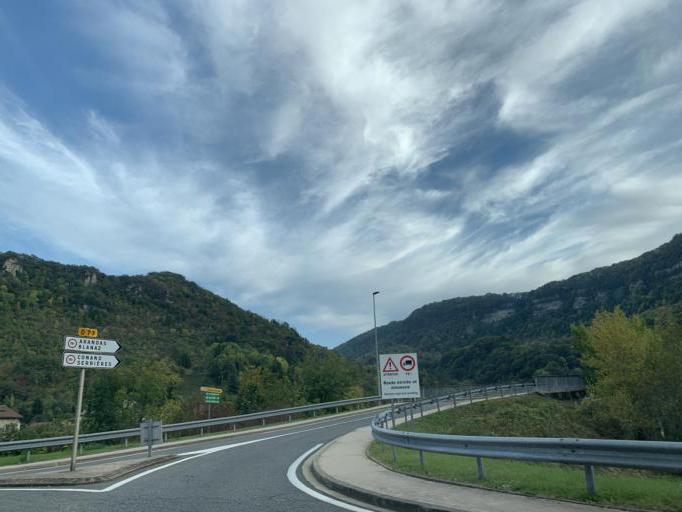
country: FR
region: Rhone-Alpes
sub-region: Departement de l'Ain
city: Saint-Rambert-en-Bugey
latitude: 45.9356
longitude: 5.4247
